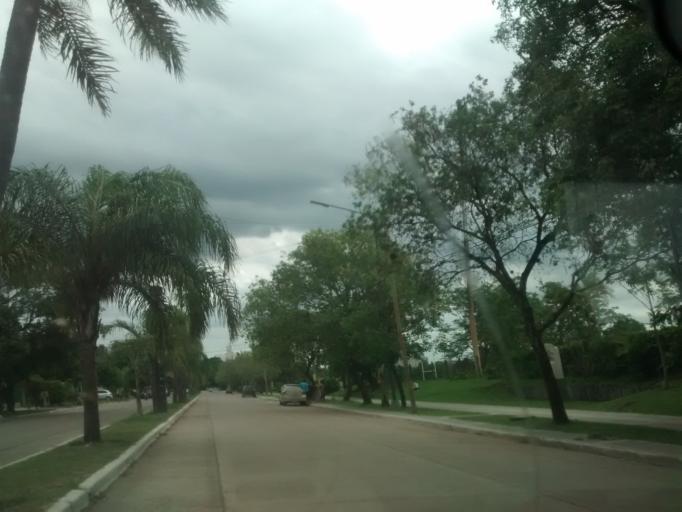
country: AR
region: Chaco
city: Resistencia
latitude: -27.4391
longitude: -58.9818
